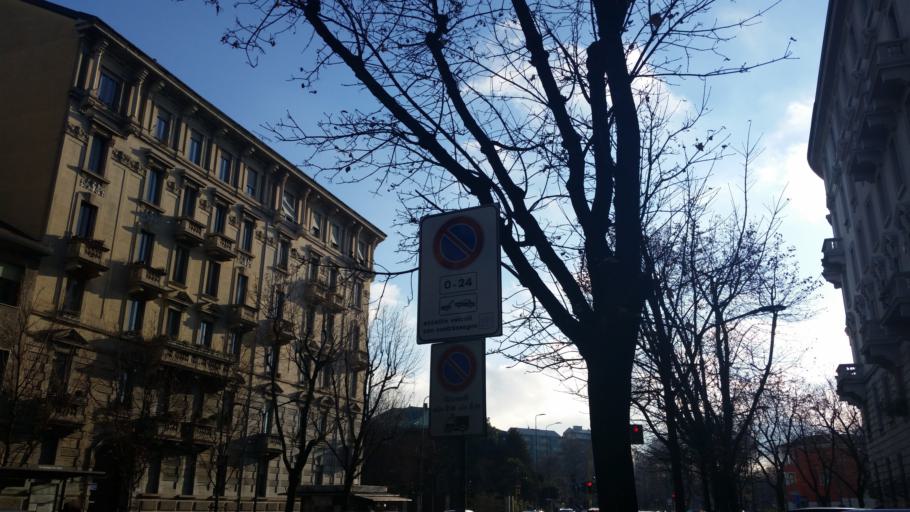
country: IT
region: Lombardy
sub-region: Citta metropolitana di Milano
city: Milano
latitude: 45.4614
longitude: 9.1503
